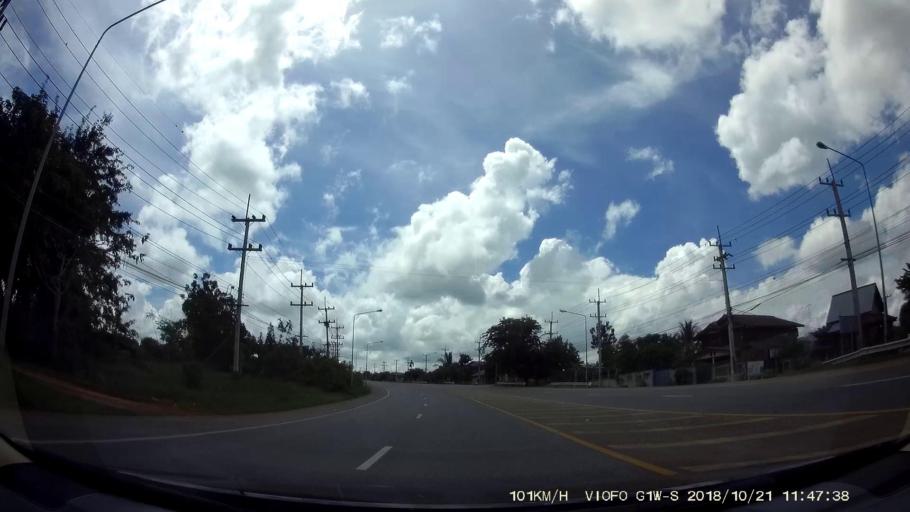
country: TH
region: Chaiyaphum
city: Noen Sa-nga
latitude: 15.6587
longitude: 101.9525
